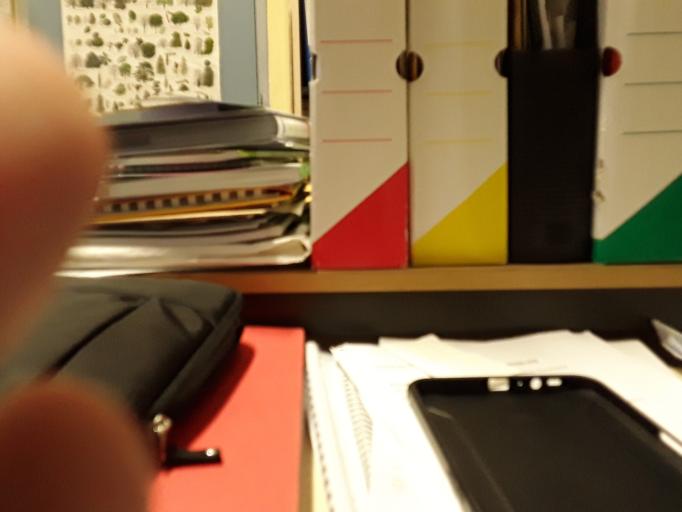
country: FR
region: Midi-Pyrenees
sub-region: Departement des Hautes-Pyrenees
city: Bagneres-de-Bigorre
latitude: 43.0515
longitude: 0.1471
